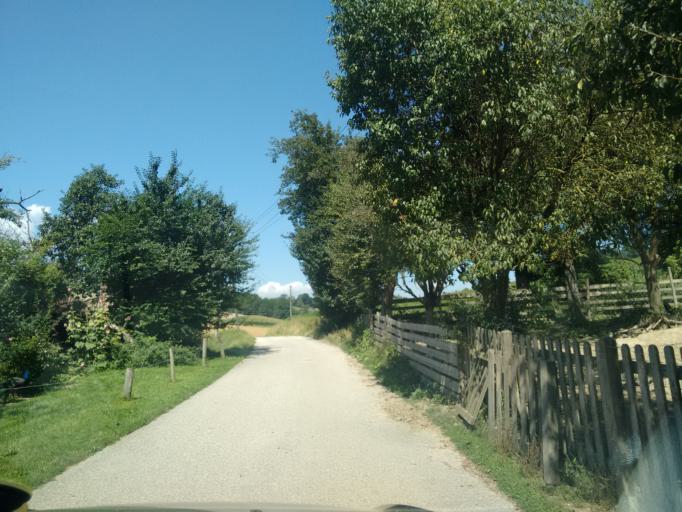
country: AT
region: Upper Austria
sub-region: Wels-Land
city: Gunskirchen
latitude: 48.1783
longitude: 13.9524
